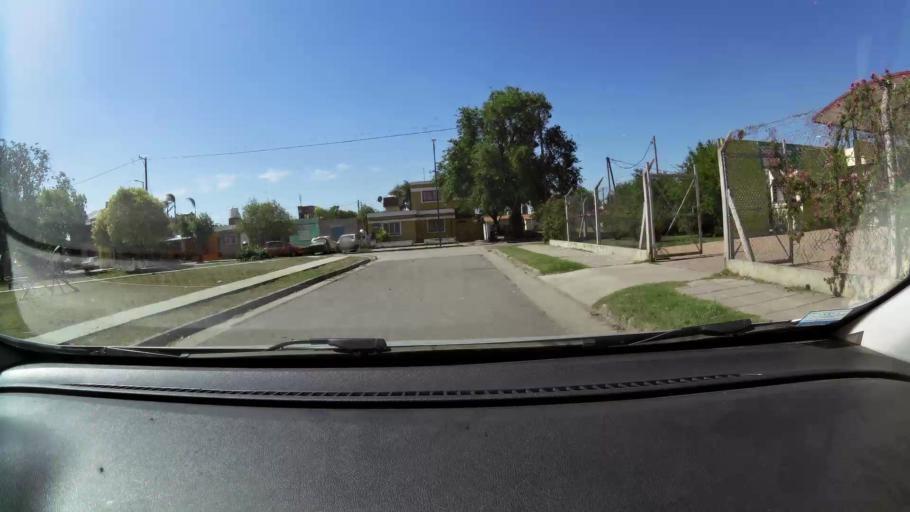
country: AR
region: Cordoba
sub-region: Departamento de Capital
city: Cordoba
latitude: -31.3671
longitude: -64.1356
